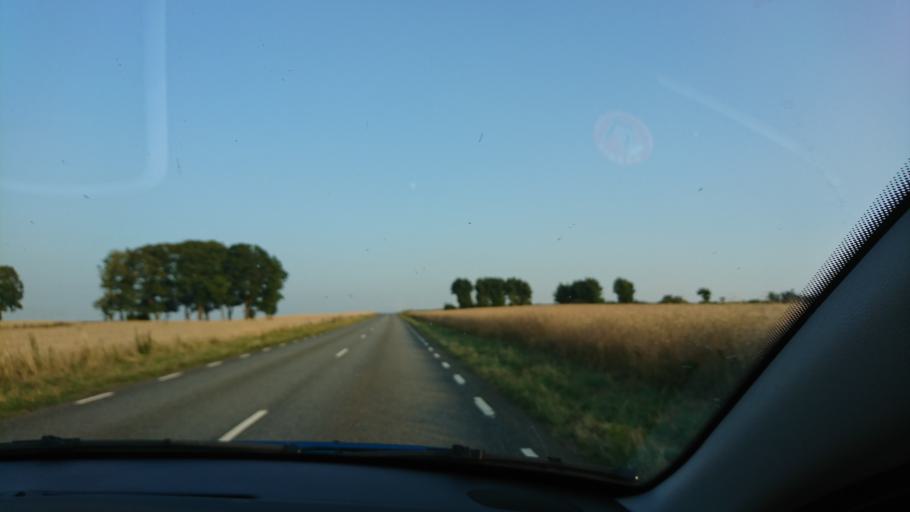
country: SE
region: Skane
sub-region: Simrishamns Kommun
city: Kivik
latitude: 55.6994
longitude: 14.1524
